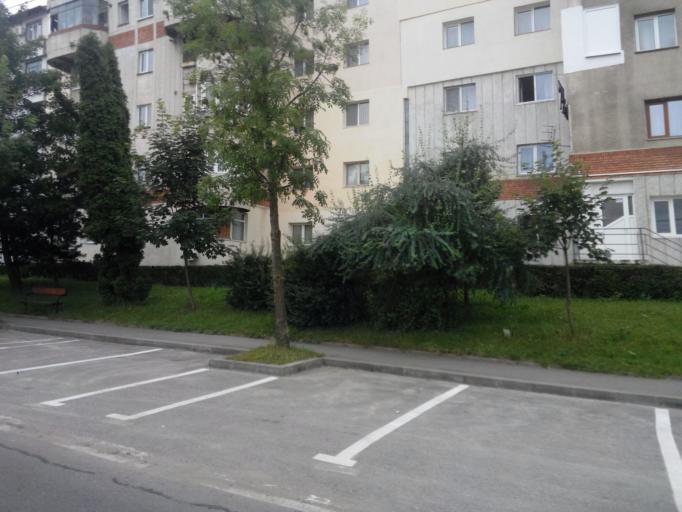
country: RO
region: Arges
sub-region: Comuna Bascov
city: Bascov
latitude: 44.8817
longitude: 24.8346
